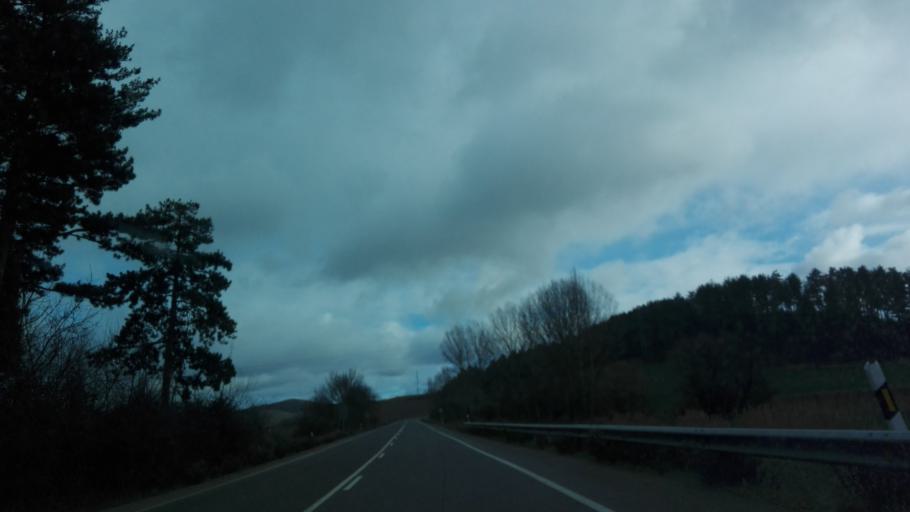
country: ES
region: Navarre
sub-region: Provincia de Navarra
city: Lizoain
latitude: 42.7979
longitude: -1.4890
